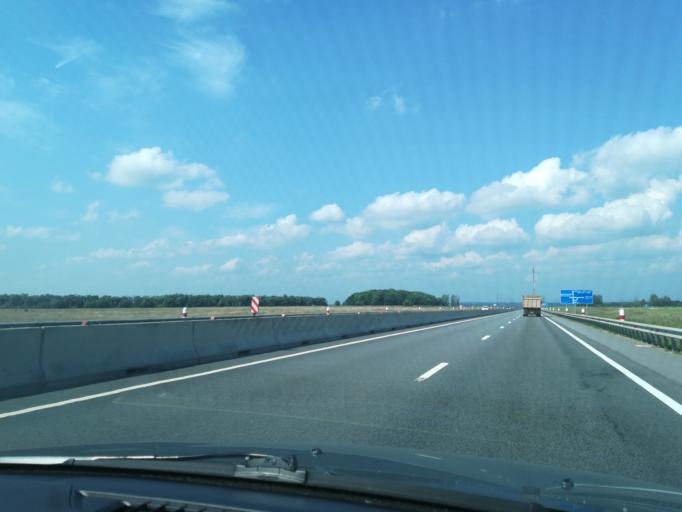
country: RU
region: Leningrad
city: Kingisepp
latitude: 59.5889
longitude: 28.7571
